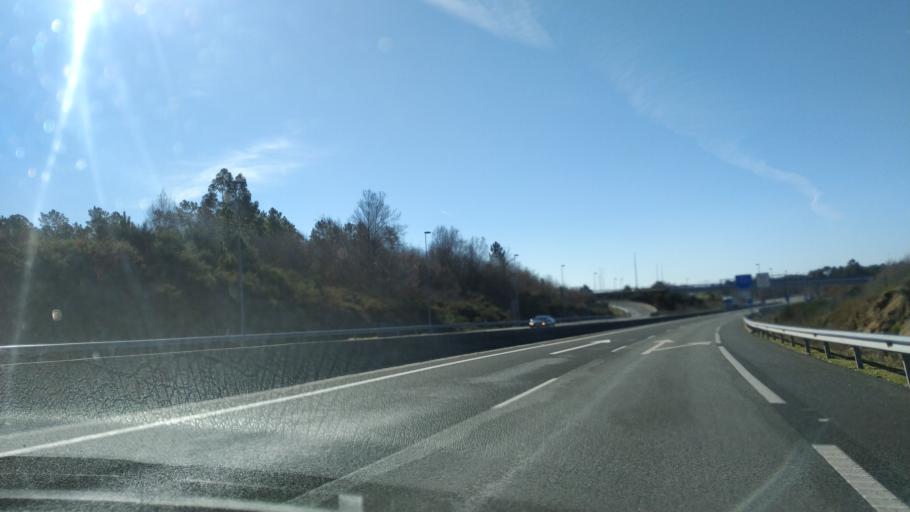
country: ES
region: Galicia
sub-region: Provincia de Ourense
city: Pinor
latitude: 42.5266
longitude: -8.0166
